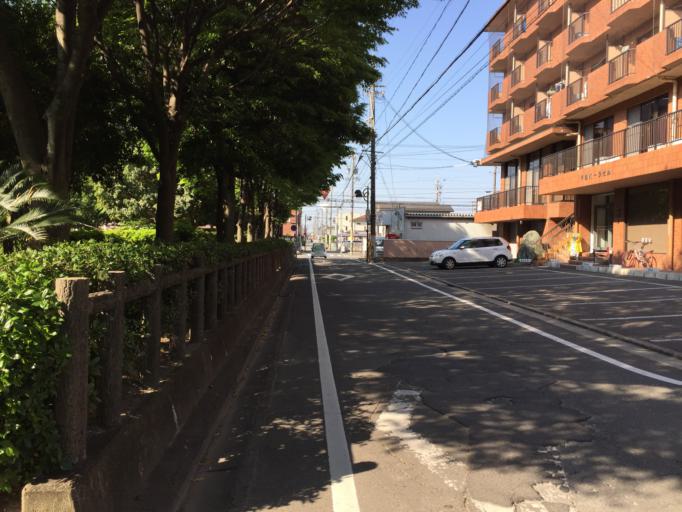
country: JP
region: Mie
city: Yokkaichi
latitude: 34.9650
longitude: 136.6155
